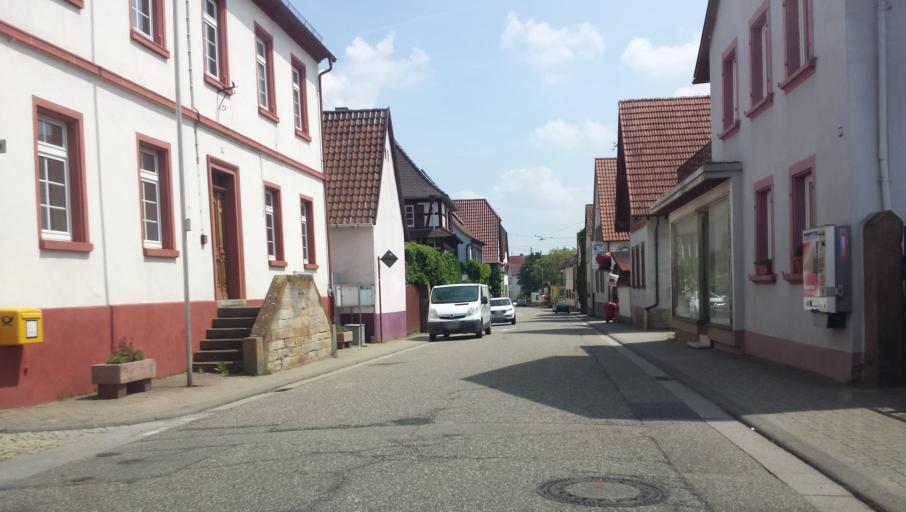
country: DE
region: Rheinland-Pfalz
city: Schweighofen
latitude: 49.0395
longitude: 7.9942
